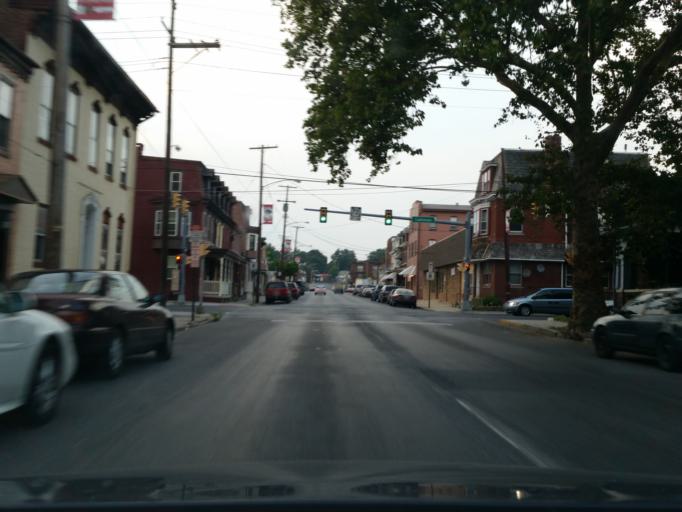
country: US
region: Pennsylvania
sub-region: Lebanon County
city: Sand Hill
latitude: 40.3452
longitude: -76.4270
